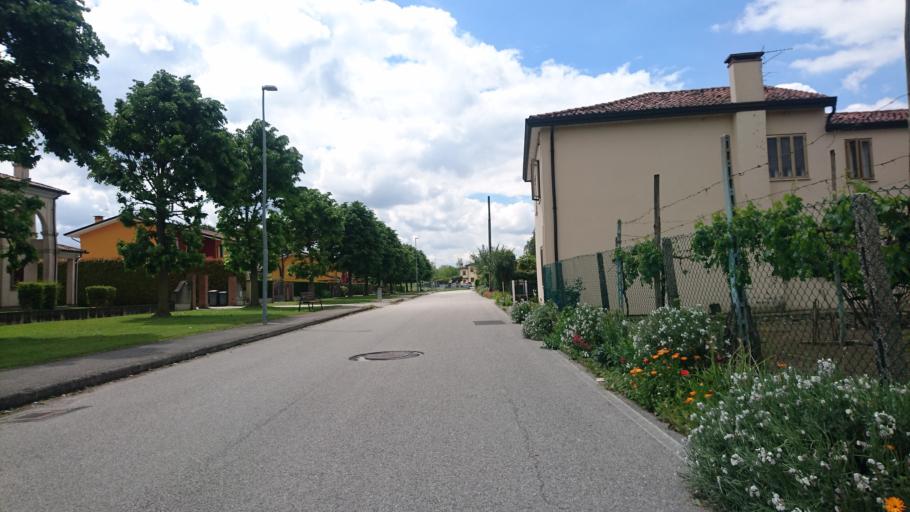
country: IT
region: Veneto
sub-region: Provincia di Padova
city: Villa Estense
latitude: 45.1474
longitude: 11.6488
